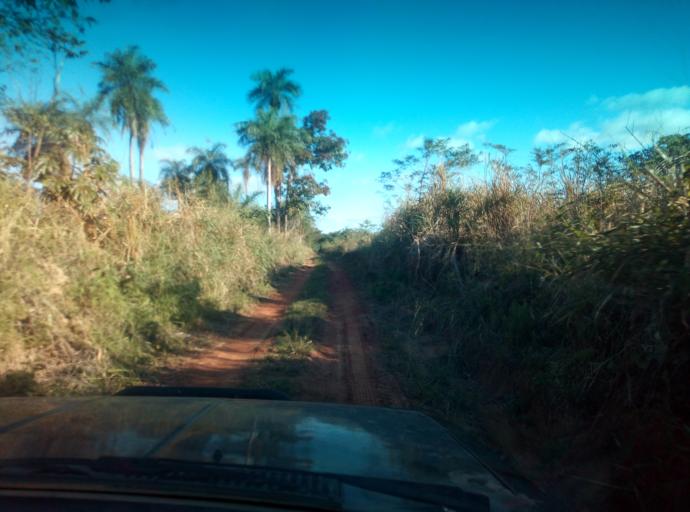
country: PY
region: Caaguazu
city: Carayao
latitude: -25.1854
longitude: -56.2625
